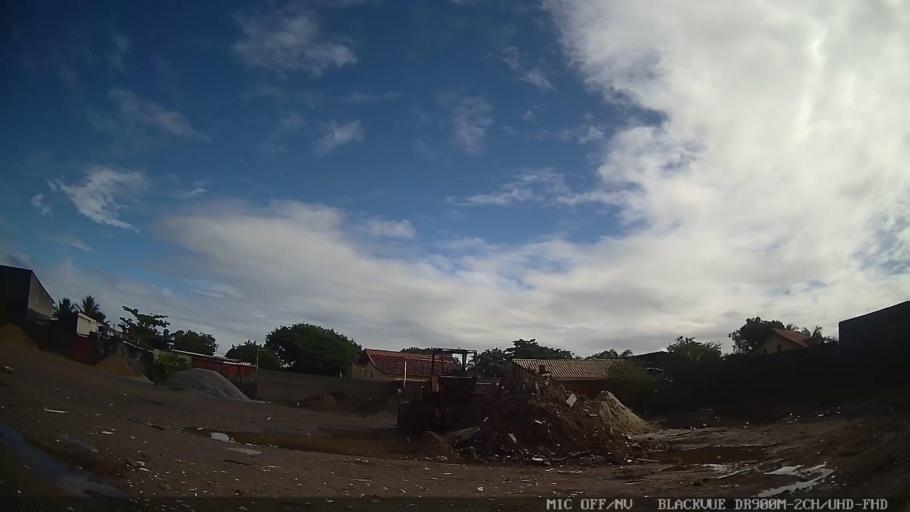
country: BR
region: Sao Paulo
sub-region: Itanhaem
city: Itanhaem
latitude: -24.2381
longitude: -46.8870
